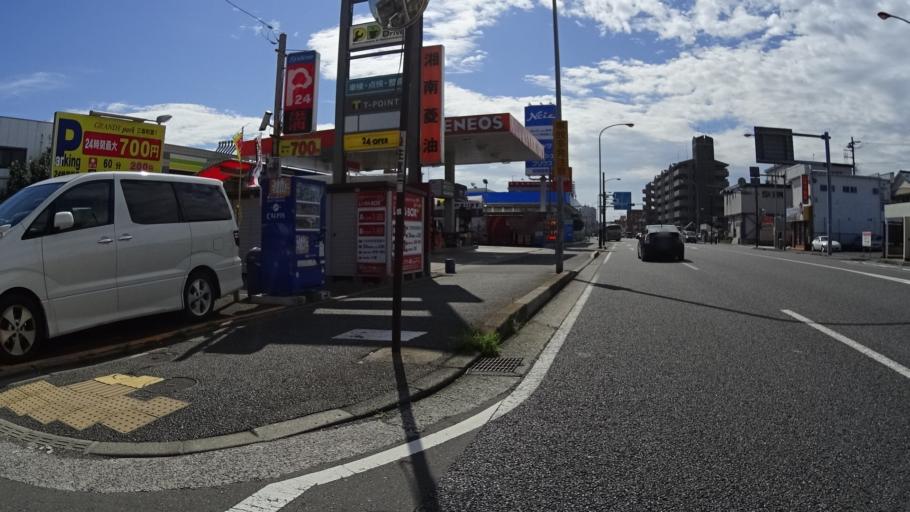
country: JP
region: Kanagawa
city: Yokosuka
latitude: 35.2655
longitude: 139.6893
